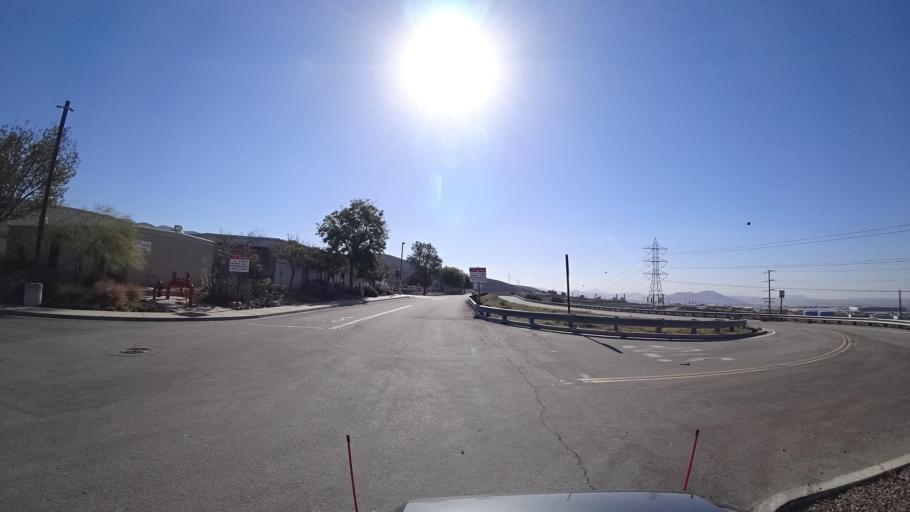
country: MX
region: Baja California
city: Tijuana
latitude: 32.5885
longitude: -116.9214
